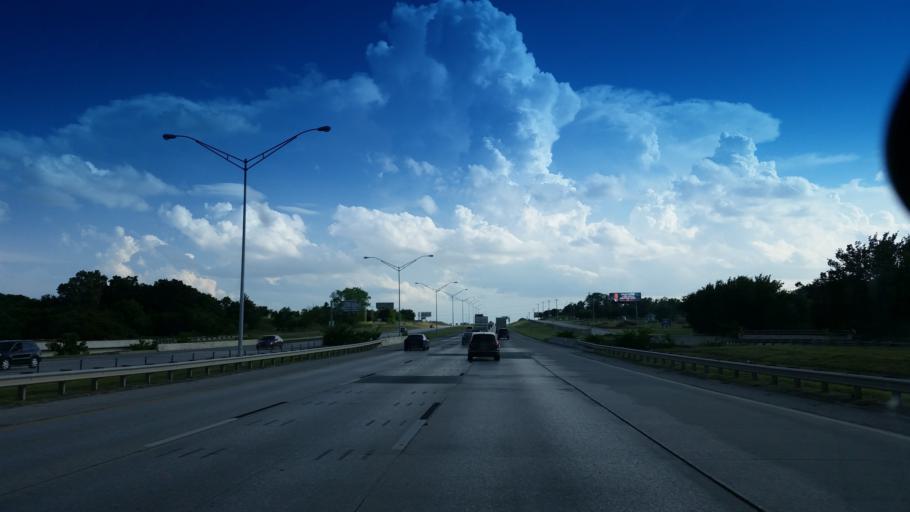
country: US
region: Oklahoma
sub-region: Oklahoma County
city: Edmond
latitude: 35.5769
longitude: -97.4445
